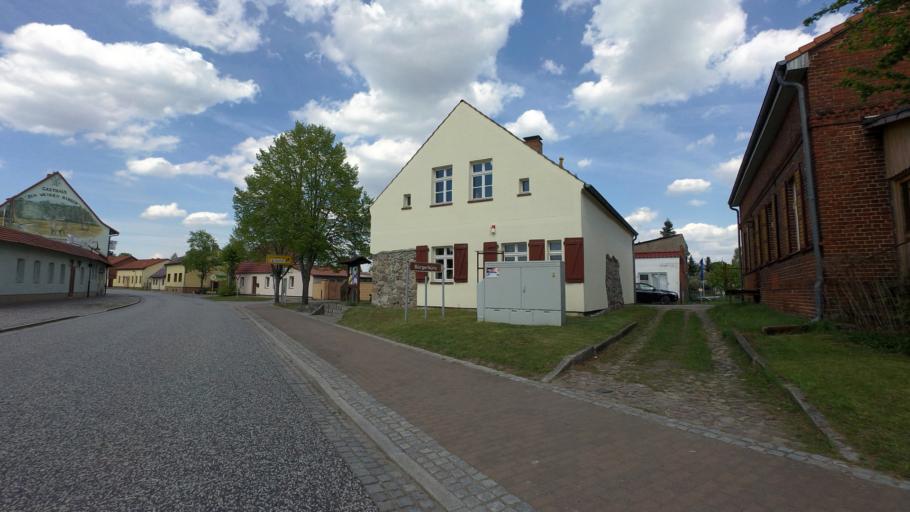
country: DE
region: Brandenburg
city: Marienwerder
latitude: 52.9047
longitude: 13.5341
